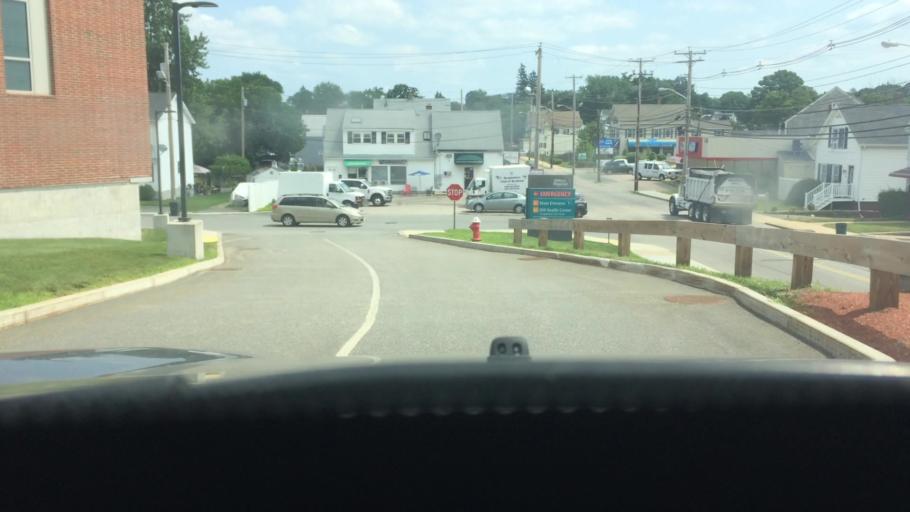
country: US
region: Massachusetts
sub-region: Worcester County
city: Milford
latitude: 42.1335
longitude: -71.5270
